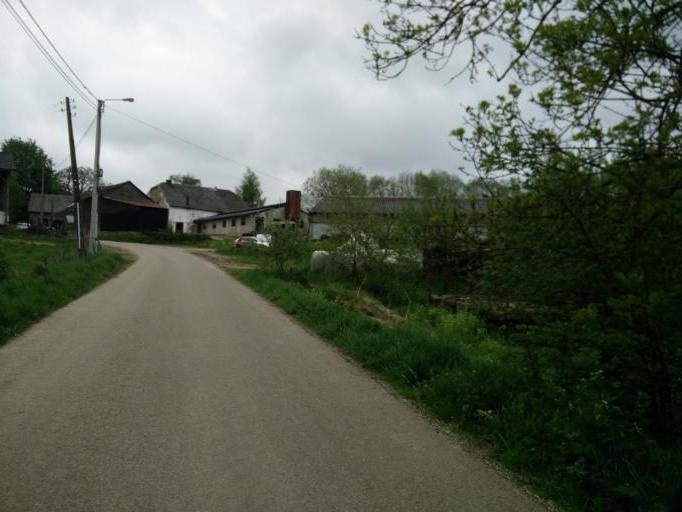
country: BE
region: Wallonia
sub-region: Province du Luxembourg
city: Houffalize
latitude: 50.1863
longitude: 5.8359
